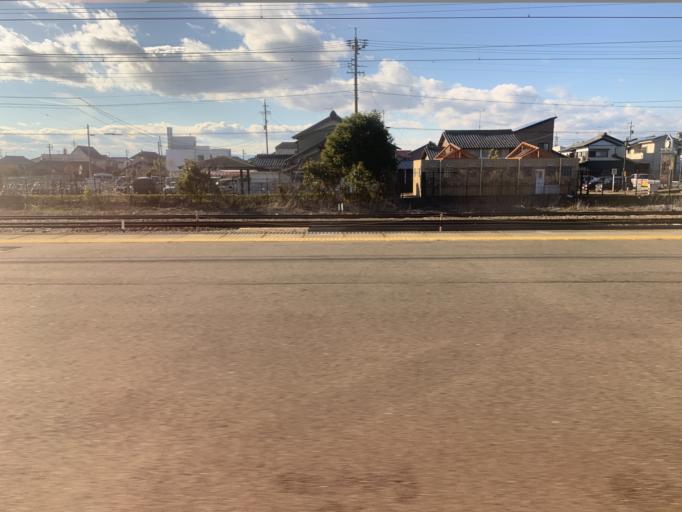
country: JP
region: Aichi
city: Kuroda
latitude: 35.3481
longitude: 136.7812
